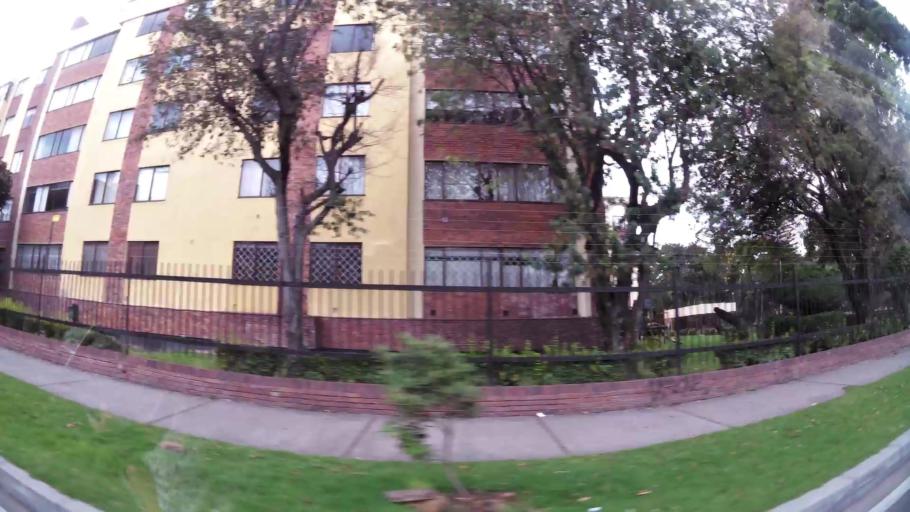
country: CO
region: Bogota D.C.
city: Barrio San Luis
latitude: 4.7295
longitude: -74.0415
